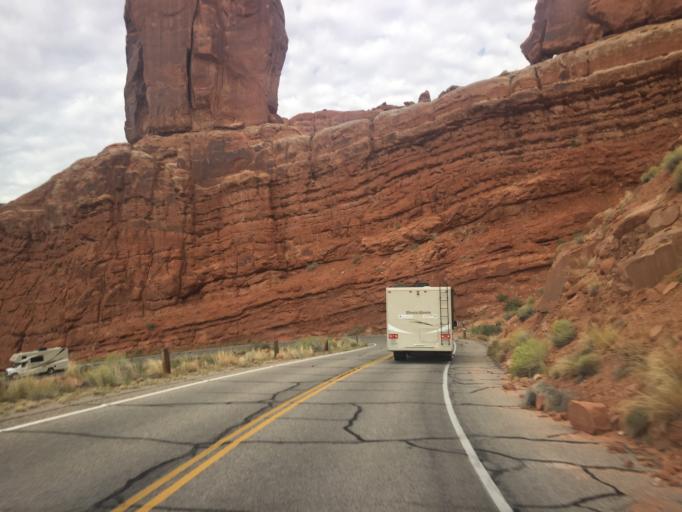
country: US
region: Utah
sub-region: Grand County
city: Moab
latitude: 38.6193
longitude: -109.6167
